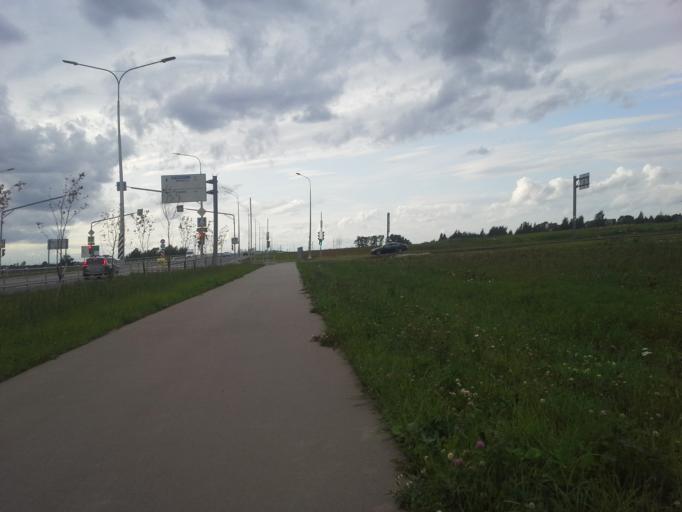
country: RU
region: Moskovskaya
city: Kokoshkino
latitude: 55.5878
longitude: 37.1597
